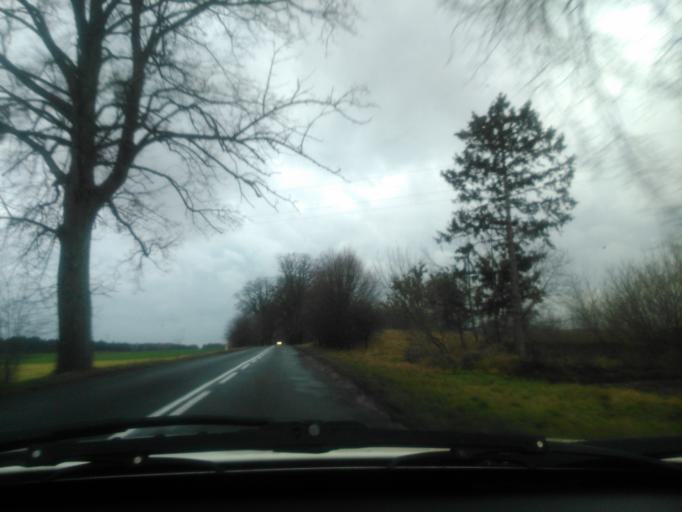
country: PL
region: Kujawsko-Pomorskie
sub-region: Powiat brodnicki
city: Gorzno
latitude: 53.2439
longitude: 19.6631
